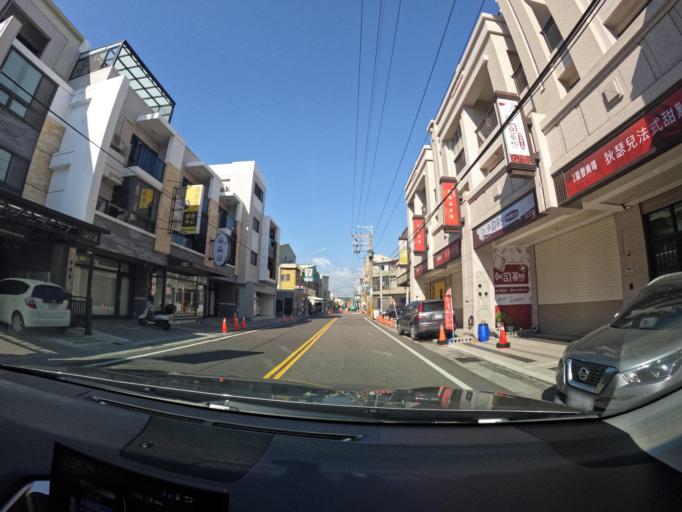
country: TW
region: Taiwan
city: Fengyuan
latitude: 24.2641
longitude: 120.5479
